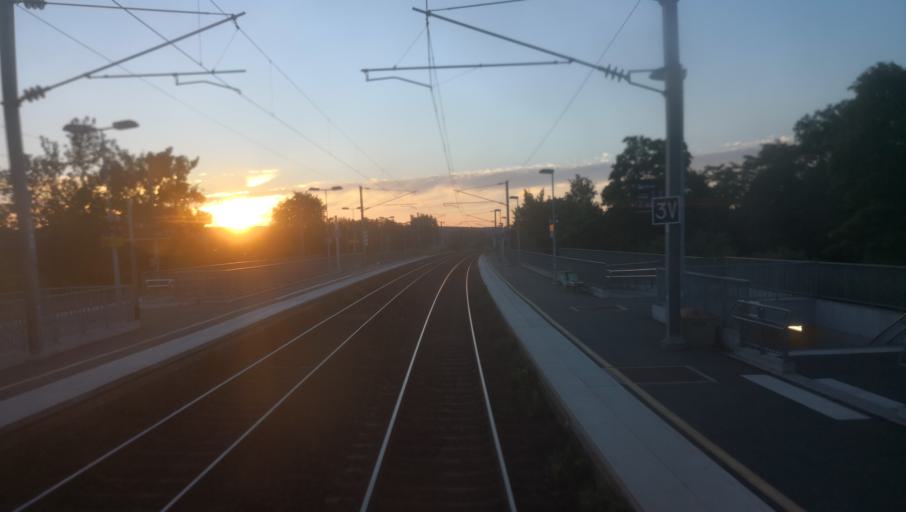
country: FR
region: Haute-Normandie
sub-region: Departement de l'Eure
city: Bueil
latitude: 48.9253
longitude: 1.4433
